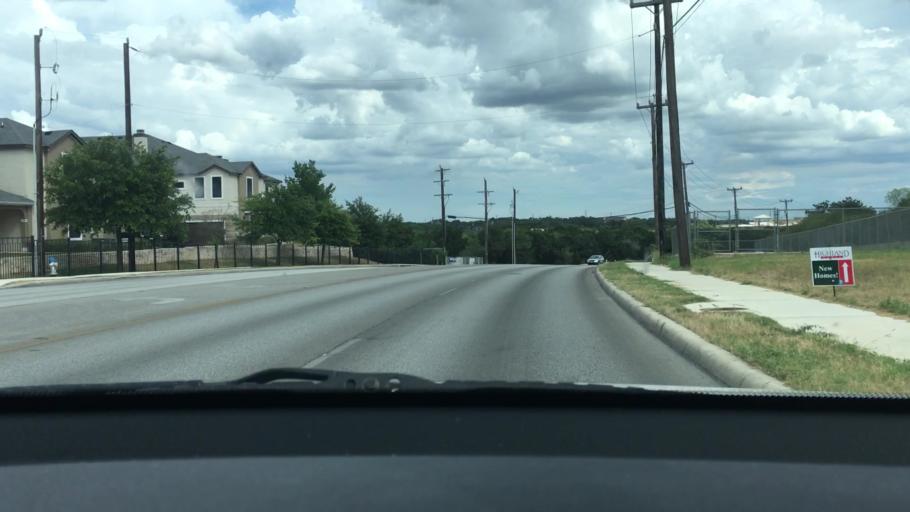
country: US
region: Texas
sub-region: Bexar County
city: Timberwood Park
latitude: 29.6529
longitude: -98.4269
